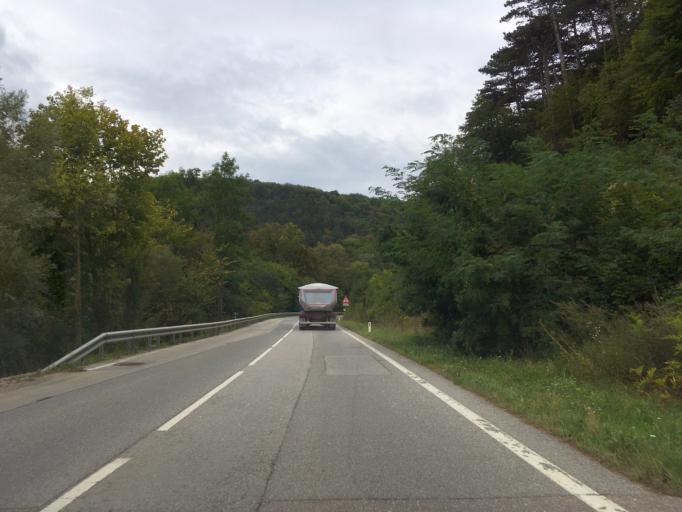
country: AT
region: Lower Austria
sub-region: Politischer Bezirk Modling
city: Gaaden
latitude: 48.0705
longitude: 16.2186
